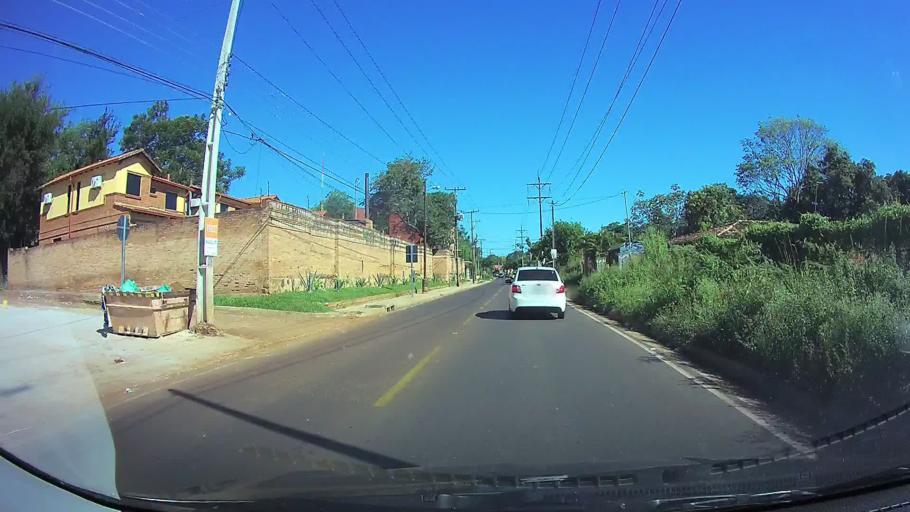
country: PY
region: Central
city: Fernando de la Mora
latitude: -25.3148
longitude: -57.5226
